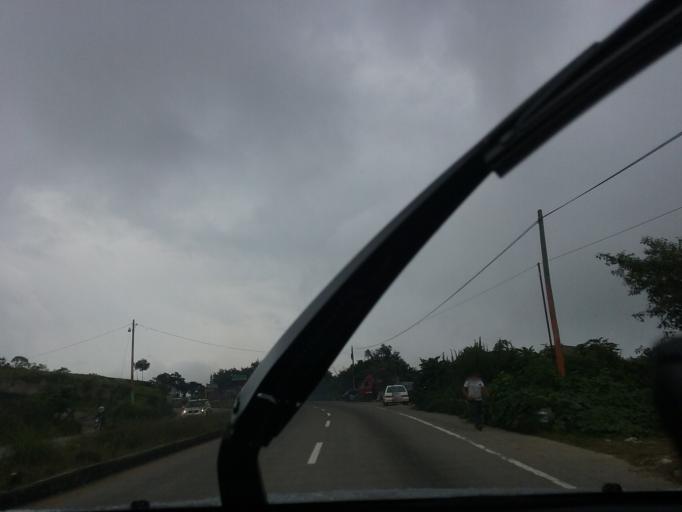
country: GT
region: Chimaltenango
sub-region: Municipio de Zaragoza
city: Zaragoza
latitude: 14.6386
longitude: -90.8891
